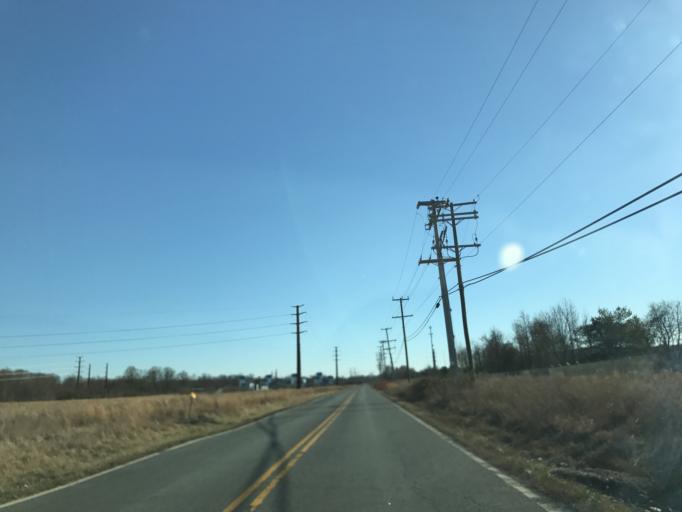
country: US
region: Maryland
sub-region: Harford County
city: Perryman
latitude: 39.4466
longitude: -76.2142
